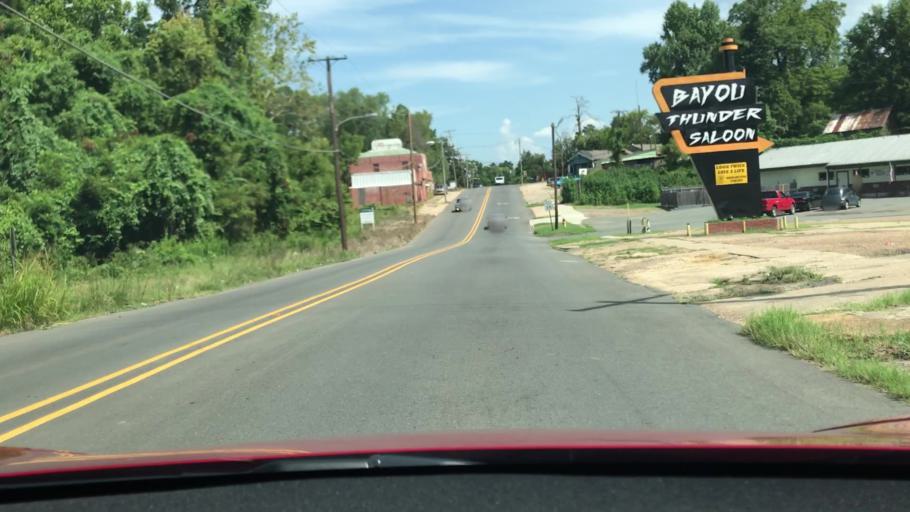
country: US
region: Louisiana
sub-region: Bossier Parish
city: Bossier City
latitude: 32.5030
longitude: -93.7360
